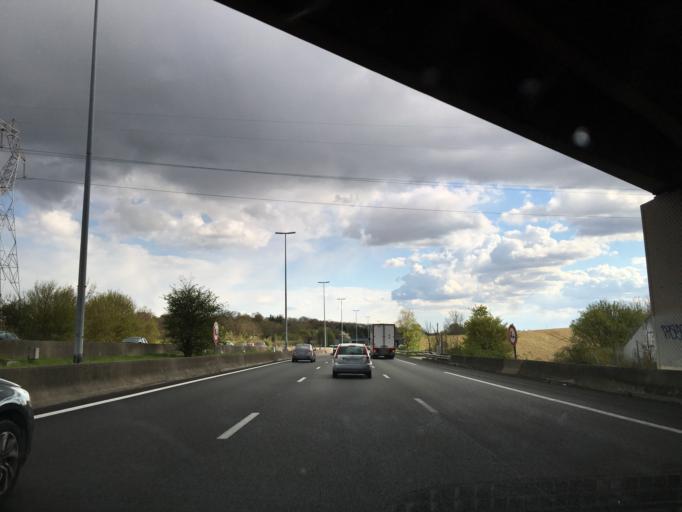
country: FR
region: Ile-de-France
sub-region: Departement du Val-d'Oise
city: Vemars
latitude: 49.0500
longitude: 2.5474
